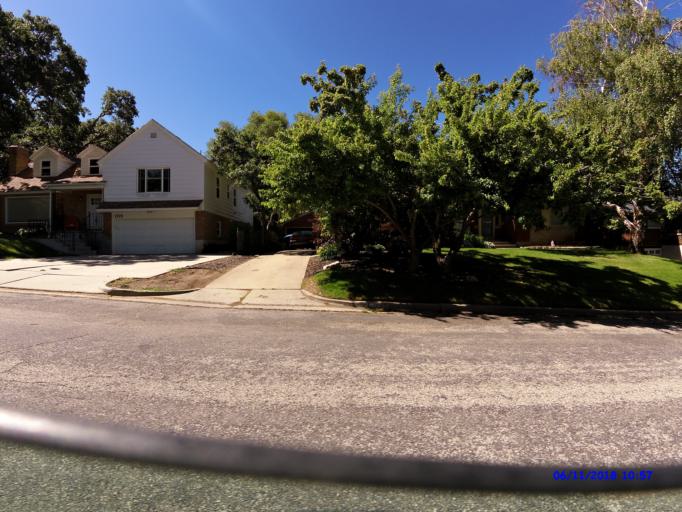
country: US
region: Utah
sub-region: Weber County
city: Ogden
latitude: 41.2160
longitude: -111.9380
